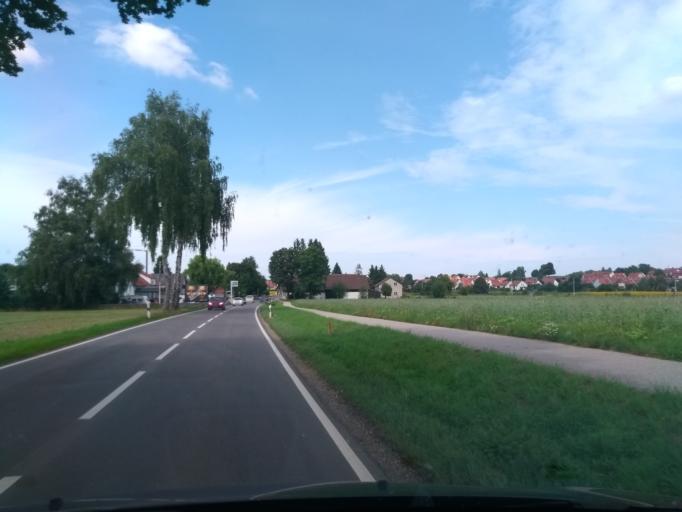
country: DE
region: Bavaria
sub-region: Upper Bavaria
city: Markt Indersdorf
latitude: 48.3479
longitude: 11.3841
